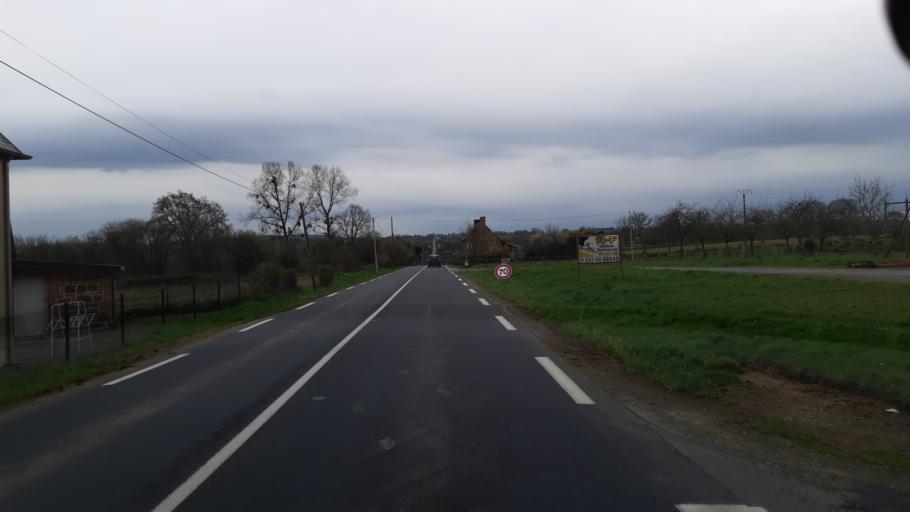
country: FR
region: Lower Normandy
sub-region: Departement de la Manche
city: Percy
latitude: 48.9836
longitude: -1.1591
